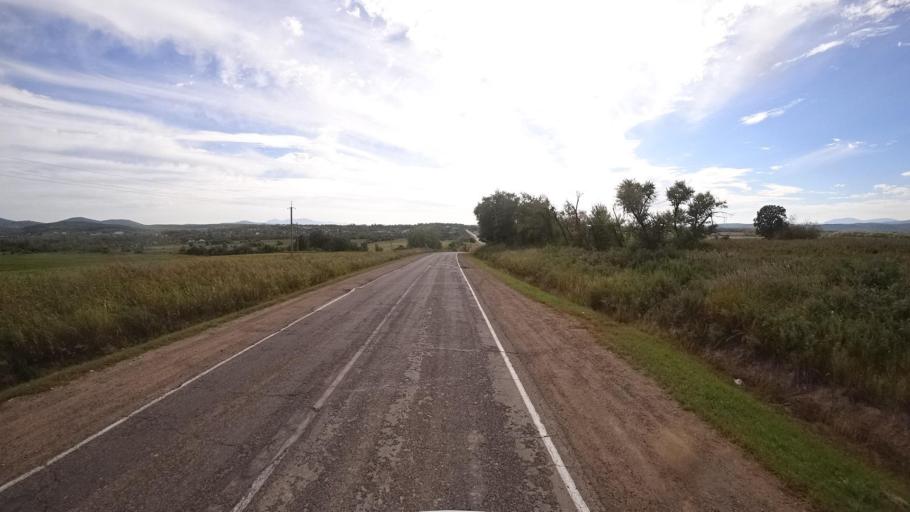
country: RU
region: Primorskiy
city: Dostoyevka
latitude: 44.3150
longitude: 133.4629
